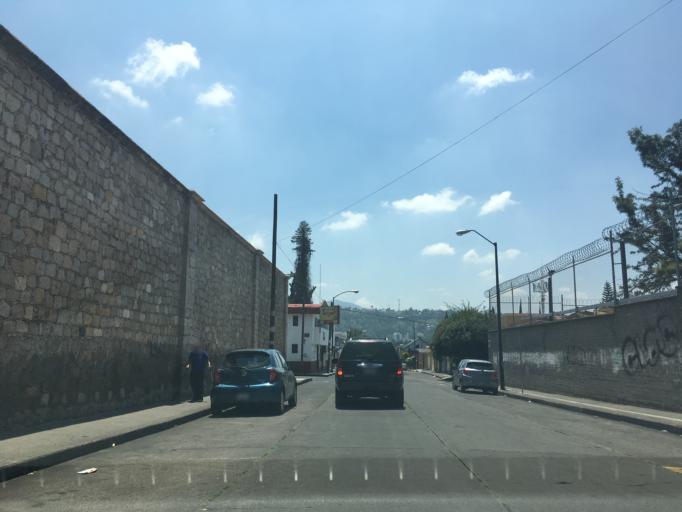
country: MX
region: Michoacan
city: Morelia
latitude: 19.6955
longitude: -101.1807
